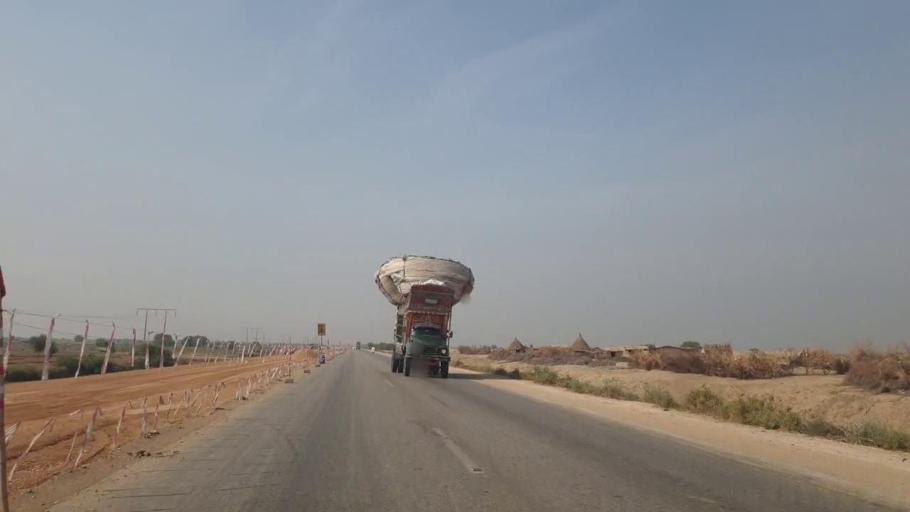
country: PK
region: Sindh
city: Sann
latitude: 26.1432
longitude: 68.0361
